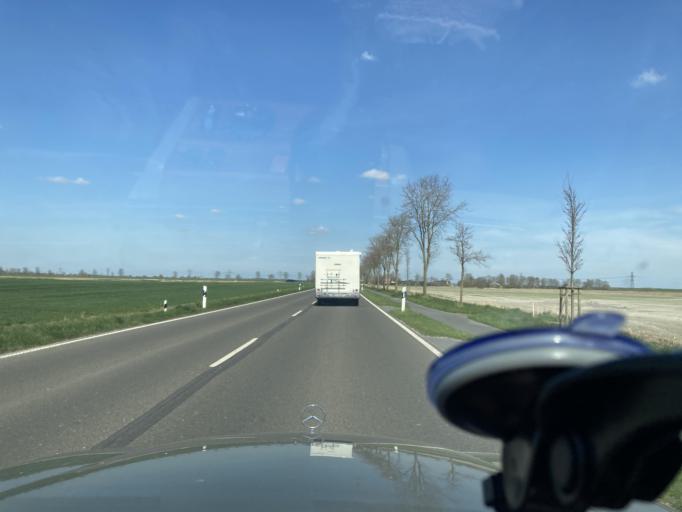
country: DE
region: Schleswig-Holstein
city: Sankt Annen
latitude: 54.3553
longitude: 9.0887
